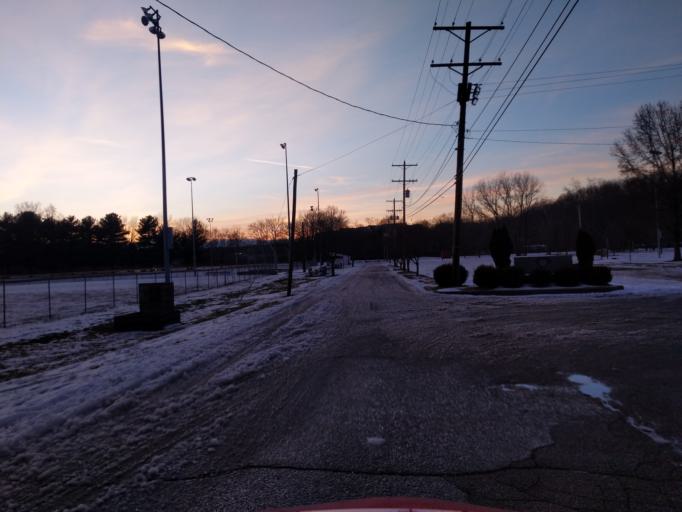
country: US
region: Ohio
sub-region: Athens County
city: Athens
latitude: 39.3341
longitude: -82.1215
